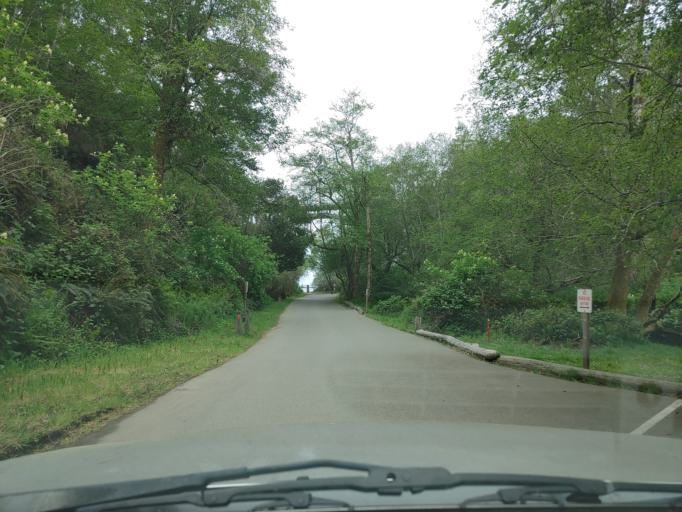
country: US
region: California
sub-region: Mendocino County
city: Fort Bragg
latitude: 39.3299
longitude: -123.8025
